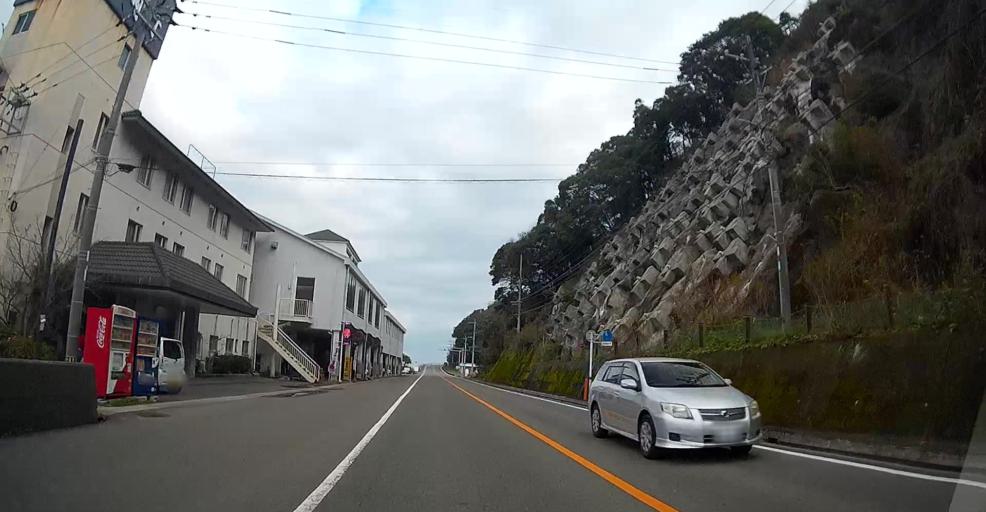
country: JP
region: Kumamoto
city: Hondo
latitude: 32.4547
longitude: 130.2141
